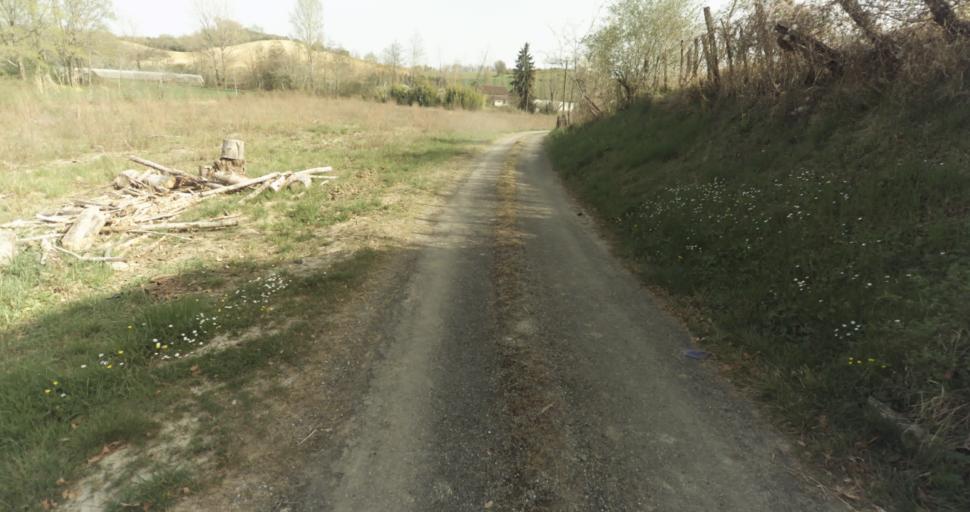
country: FR
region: Midi-Pyrenees
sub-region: Departement du Tarn-et-Garonne
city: Lafrancaise
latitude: 44.1457
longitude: 1.1778
